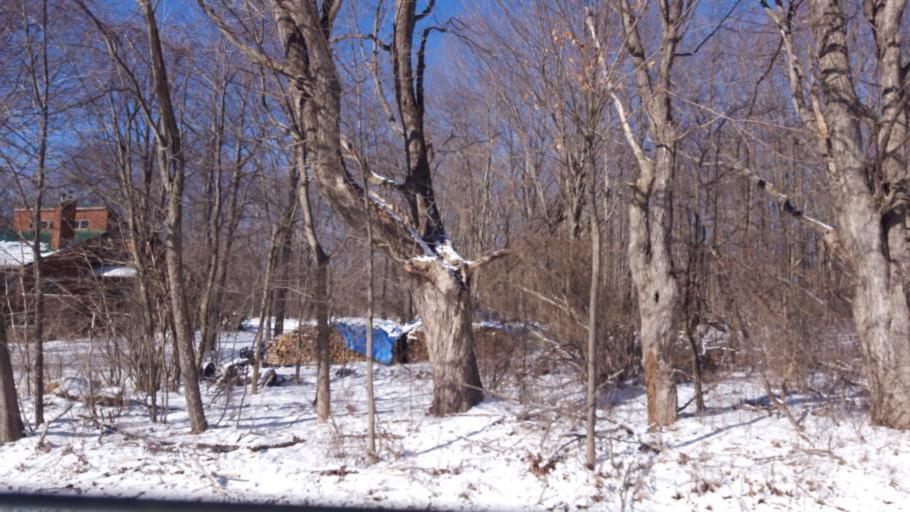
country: US
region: New York
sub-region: Allegany County
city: Wellsville
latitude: 42.1466
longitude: -77.9317
